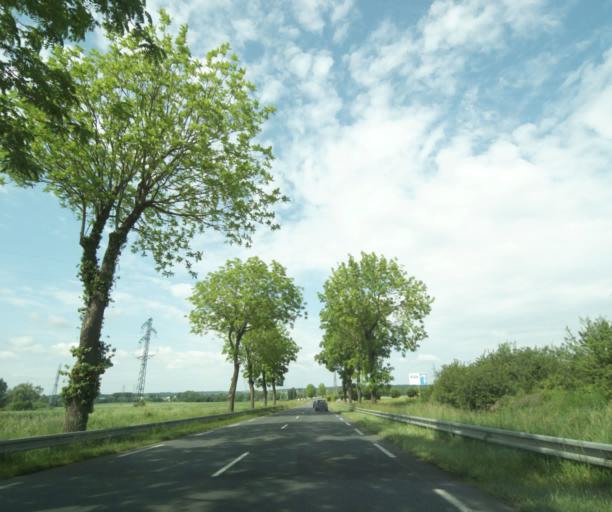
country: FR
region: Pays de la Loire
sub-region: Departement de Maine-et-Loire
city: Distre
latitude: 47.2076
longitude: -0.1192
